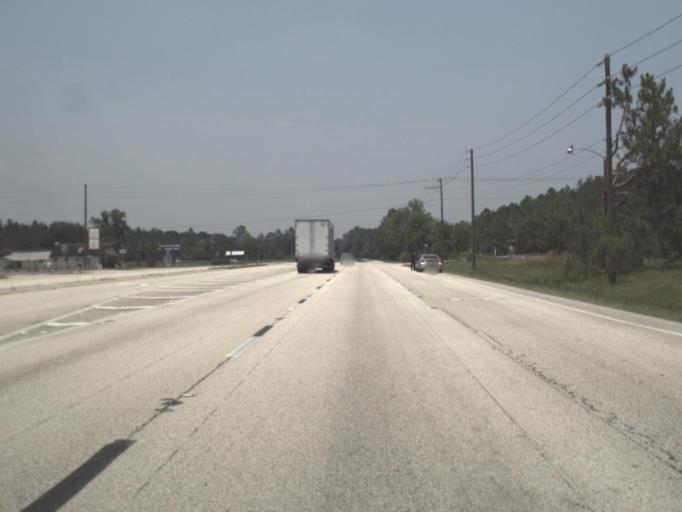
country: US
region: Florida
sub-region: Bradford County
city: Starke
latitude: 30.0544
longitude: -82.0682
